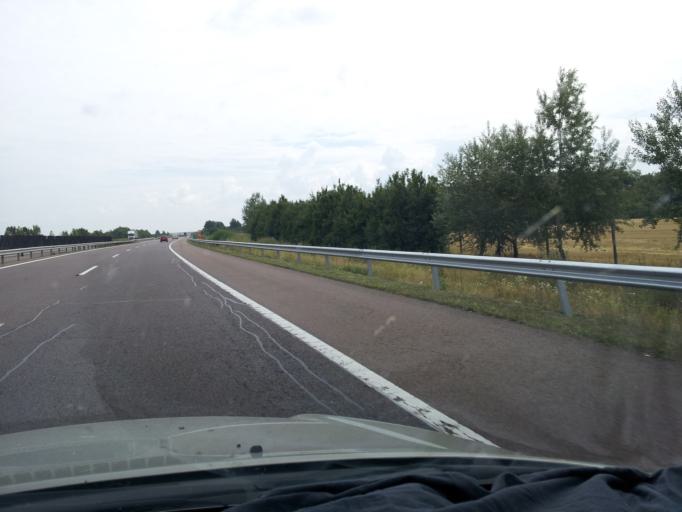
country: HU
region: Heves
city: Szihalom
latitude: 47.7532
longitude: 20.4597
